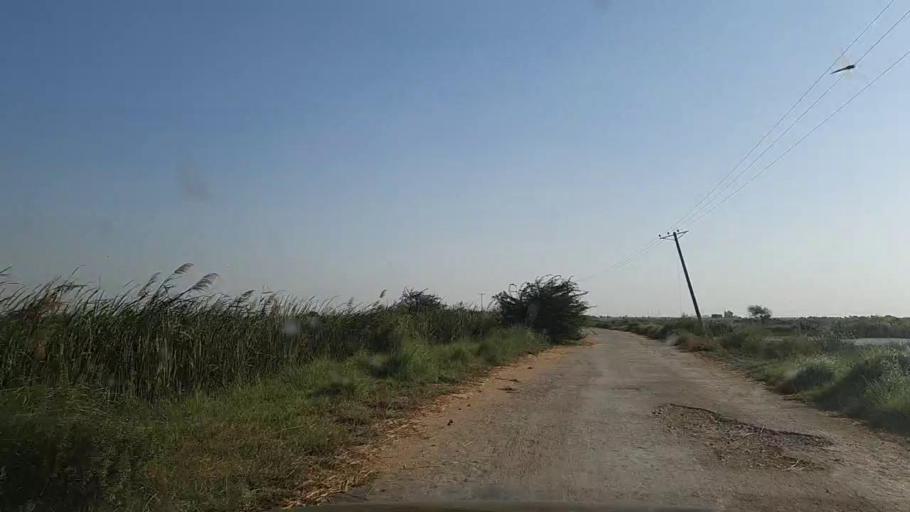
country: PK
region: Sindh
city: Thatta
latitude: 24.6421
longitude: 68.0752
